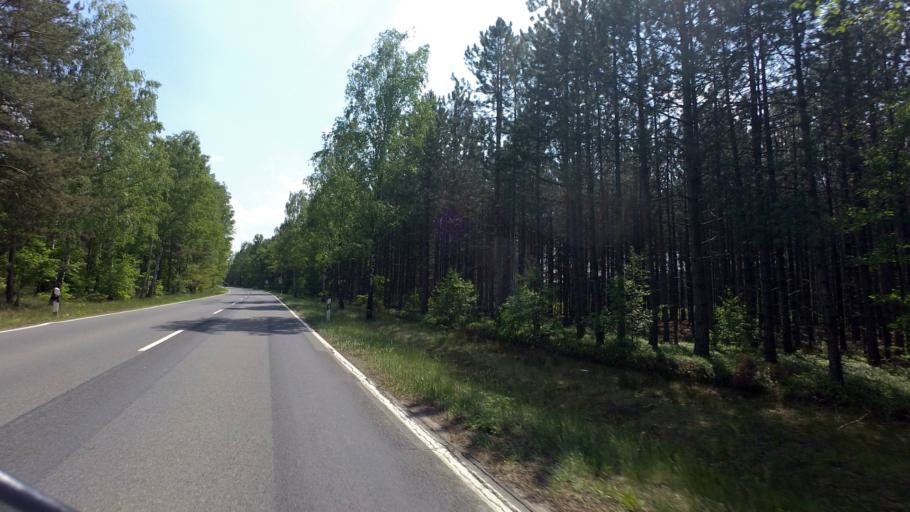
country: DE
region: Saxony
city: Schleife
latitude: 51.5594
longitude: 14.4944
